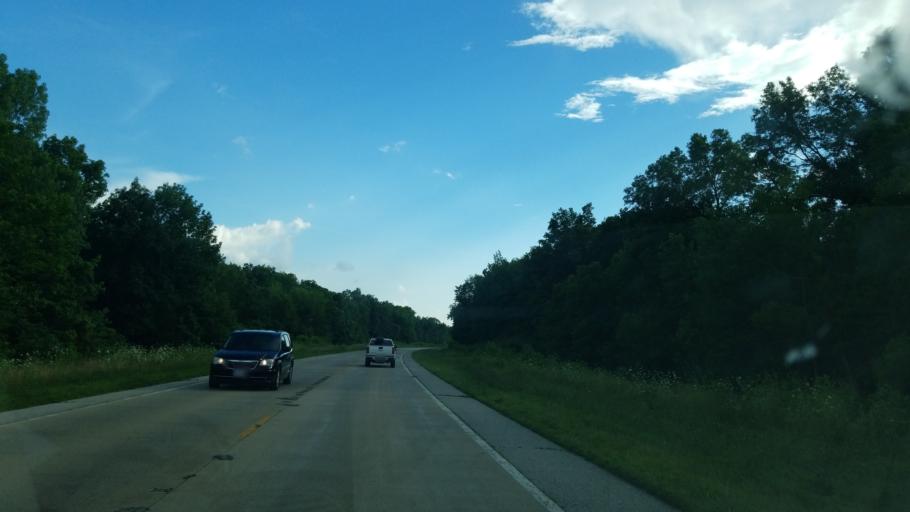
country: US
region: Illinois
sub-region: Marion County
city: Central City
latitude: 38.5707
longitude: -89.1111
